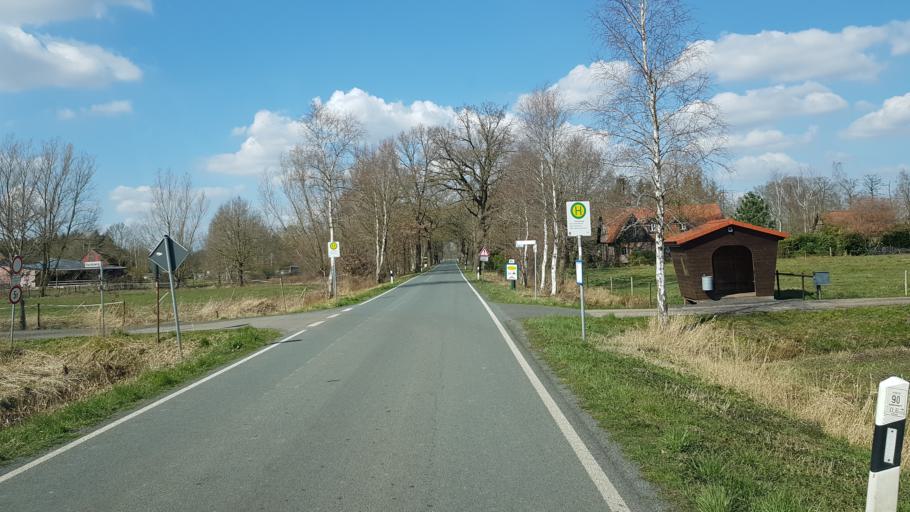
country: DE
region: Lower Saxony
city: Rastede
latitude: 53.3139
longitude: 8.2320
